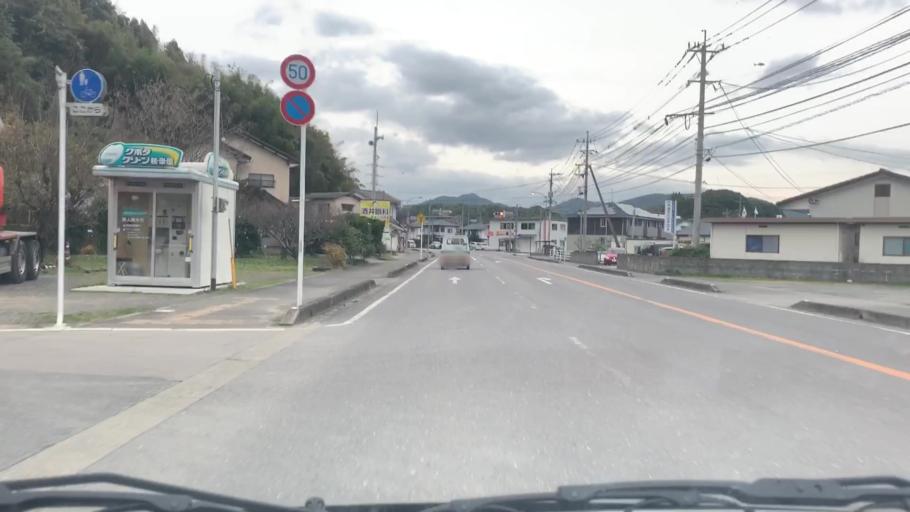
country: JP
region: Saga Prefecture
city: Takeocho-takeo
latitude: 33.1852
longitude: 130.0379
